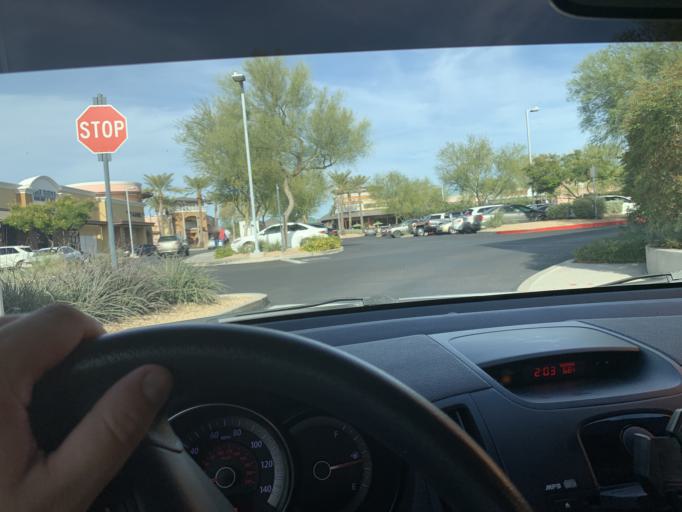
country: US
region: Arizona
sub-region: Maricopa County
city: Anthem
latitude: 33.7135
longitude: -112.1116
